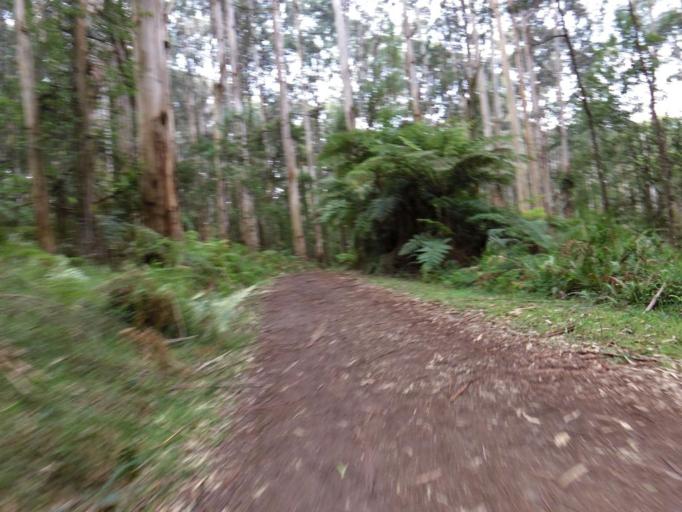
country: AU
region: Victoria
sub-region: Yarra Ranges
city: Mount Dandenong
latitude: -37.8375
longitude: 145.3855
